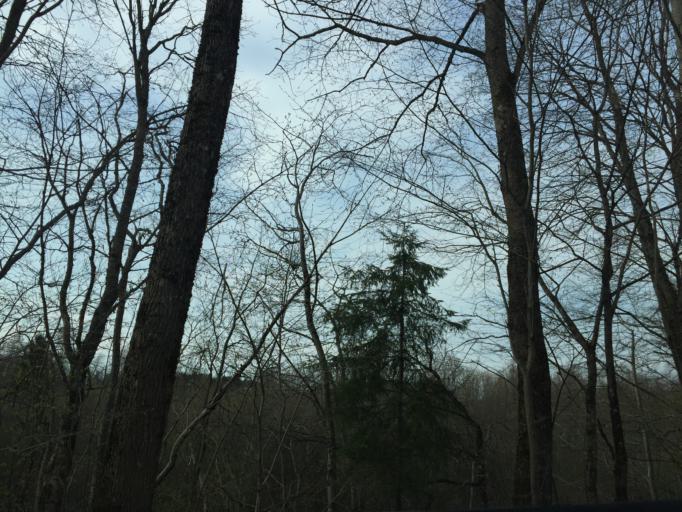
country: EE
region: Vorumaa
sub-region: Voru linn
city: Voru
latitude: 57.7174
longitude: 27.0568
